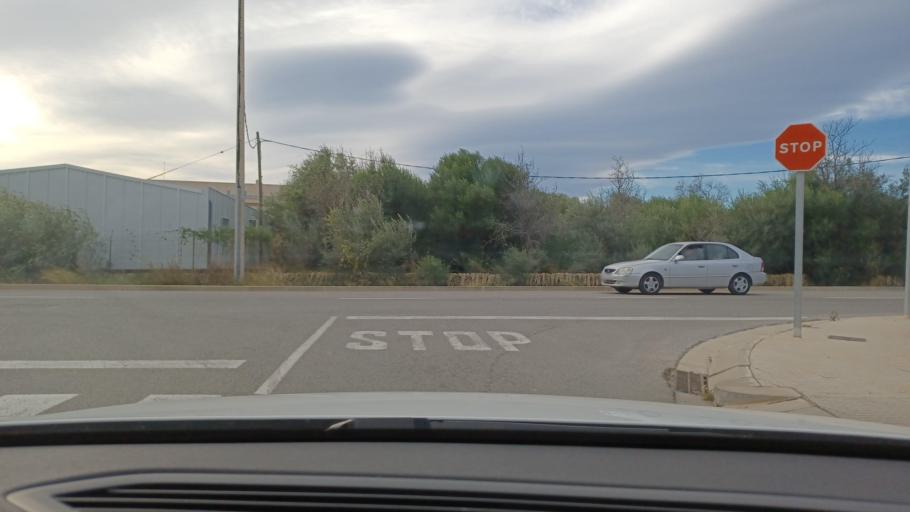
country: ES
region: Catalonia
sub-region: Provincia de Tarragona
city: Amposta
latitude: 40.7081
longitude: 0.5701
